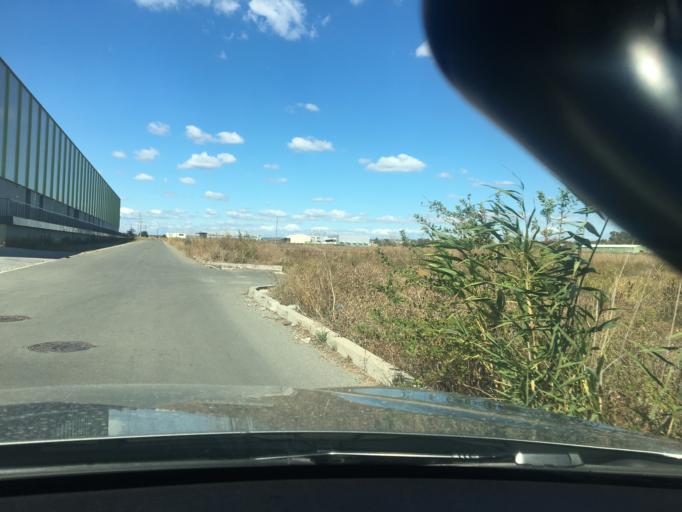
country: BG
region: Burgas
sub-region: Obshtina Burgas
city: Burgas
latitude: 42.5339
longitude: 27.4532
